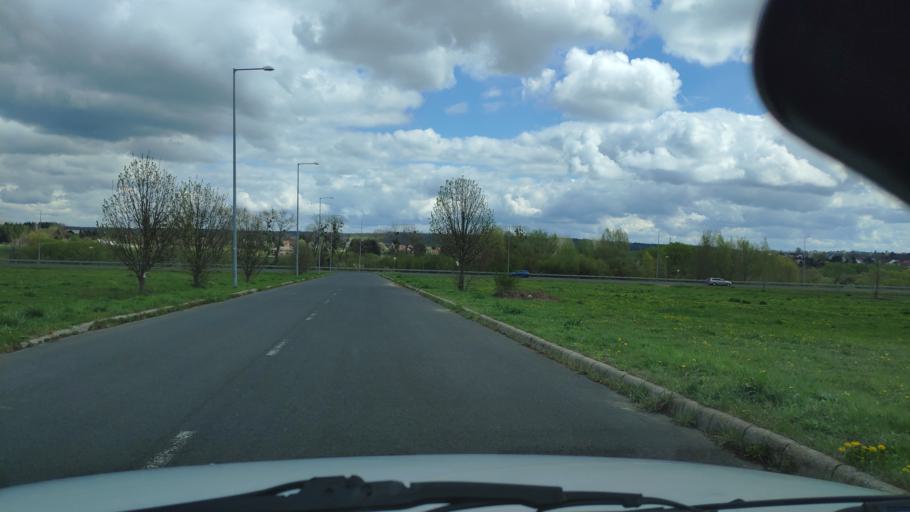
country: HU
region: Zala
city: Nagykanizsa
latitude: 46.4559
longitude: 17.0158
